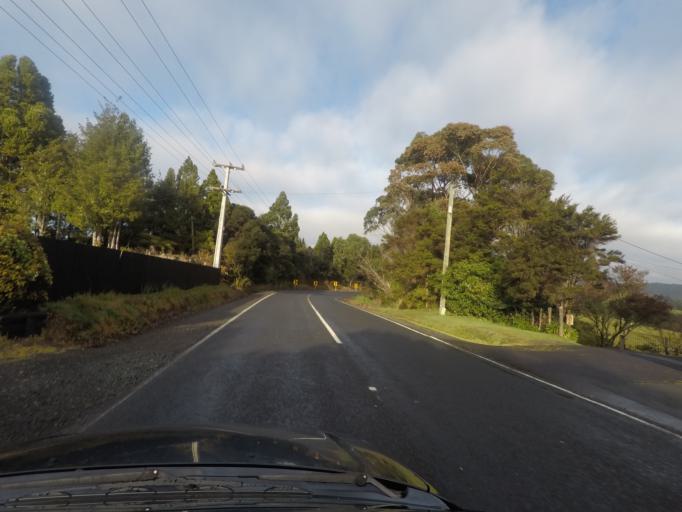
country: NZ
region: Auckland
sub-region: Auckland
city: Waitakere
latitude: -36.9130
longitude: 174.6054
